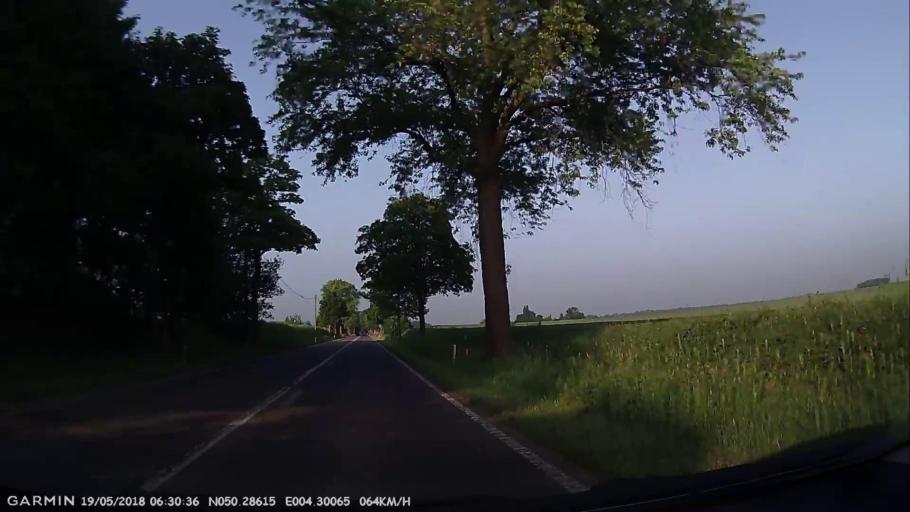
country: BE
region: Wallonia
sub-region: Province du Hainaut
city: Thuin
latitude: 50.2861
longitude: 4.3006
